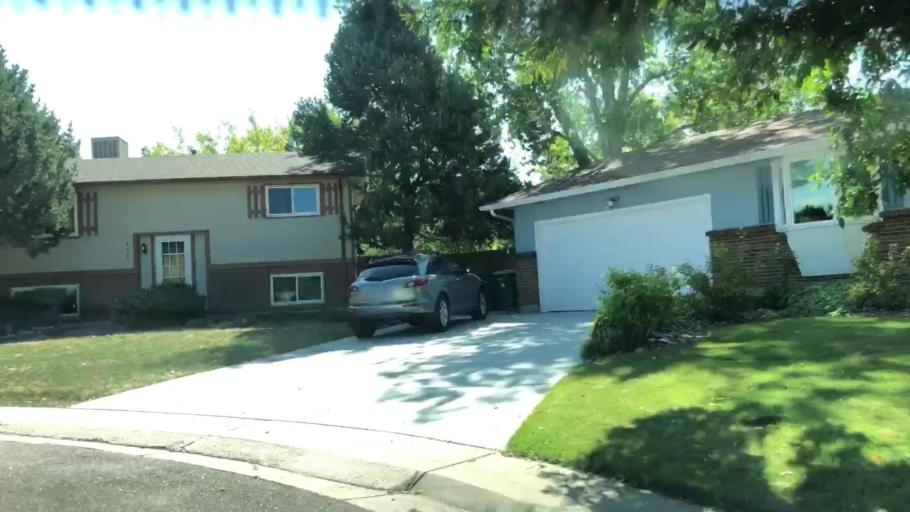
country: US
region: Colorado
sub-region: Douglas County
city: Acres Green
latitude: 39.5601
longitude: -104.8942
